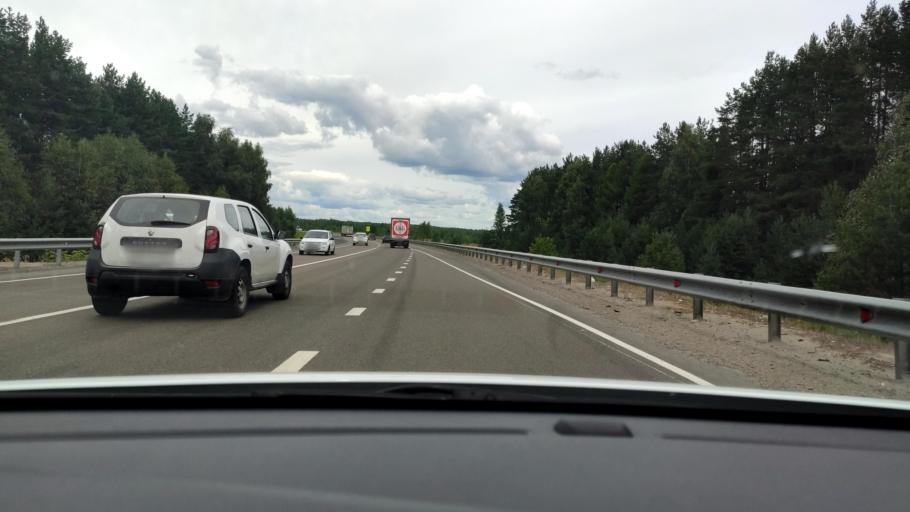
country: RU
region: Mariy-El
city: Pomary
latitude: 55.9245
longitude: 48.3746
